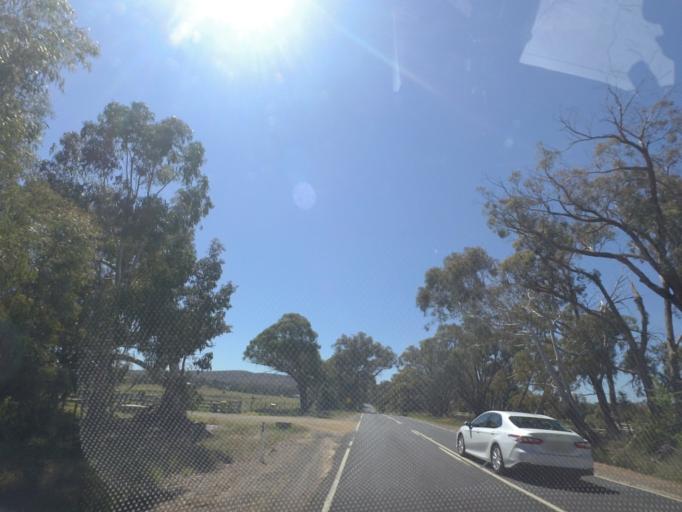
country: AU
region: Victoria
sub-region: Hume
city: Sunbury
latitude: -37.2520
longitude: 144.7389
